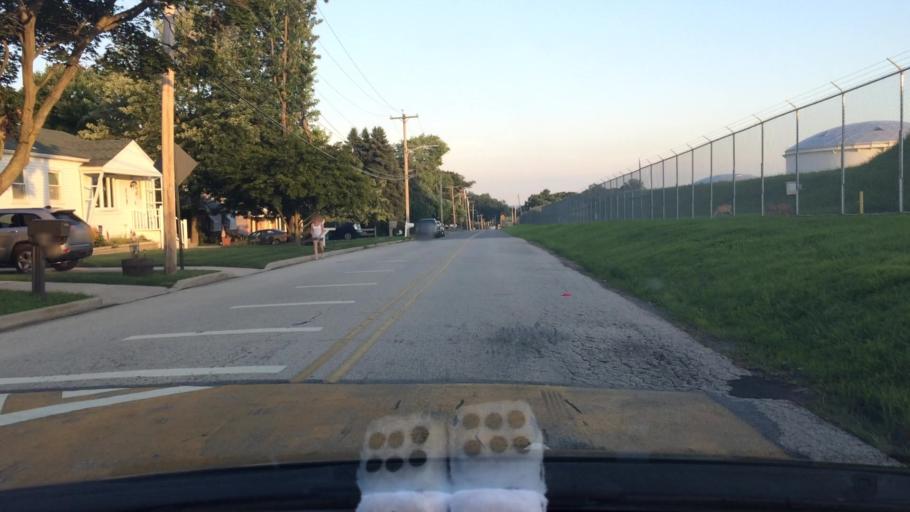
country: US
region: Pennsylvania
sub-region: Delaware County
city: Village Green-Green Ridge
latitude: 39.8683
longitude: -75.4542
